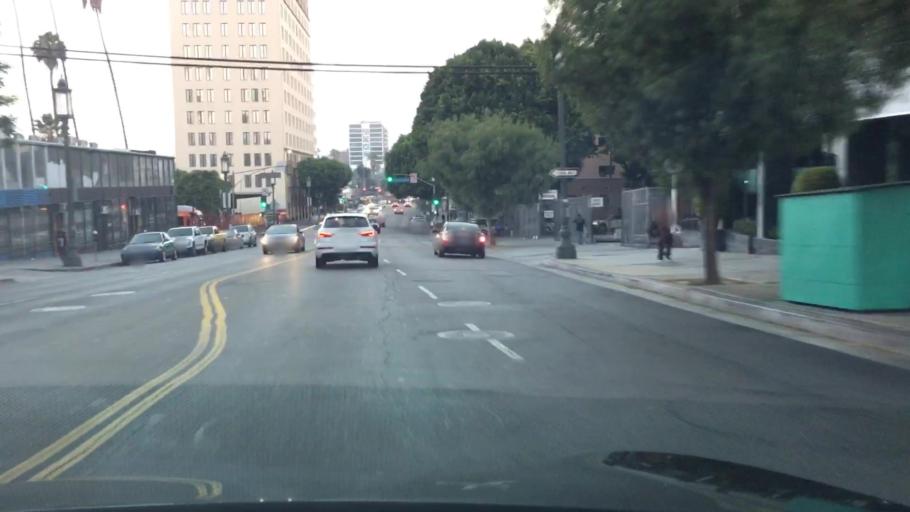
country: US
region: California
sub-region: Los Angeles County
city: Echo Park
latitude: 34.0566
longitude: -118.2727
